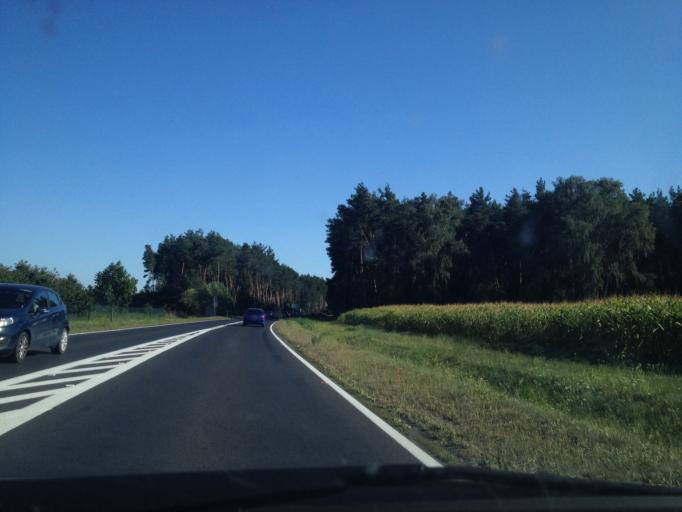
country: PL
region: Greater Poland Voivodeship
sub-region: Powiat poznanski
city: Kornik
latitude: 52.2252
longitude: 17.0718
